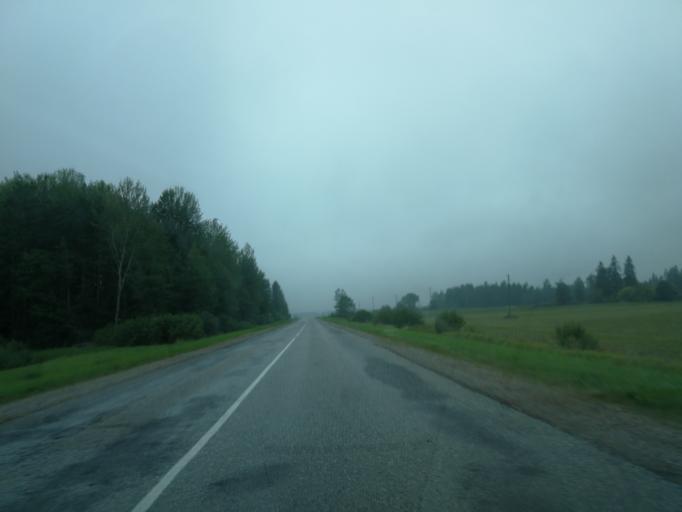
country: LV
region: Varkava
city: Vecvarkava
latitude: 56.3135
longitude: 26.5267
